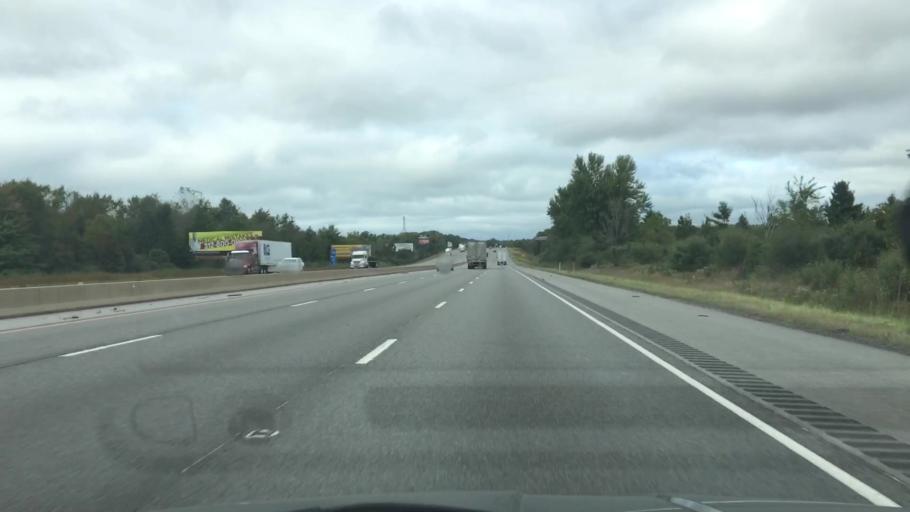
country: US
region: Indiana
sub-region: LaPorte County
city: Trail Creek
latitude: 41.7114
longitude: -86.8057
